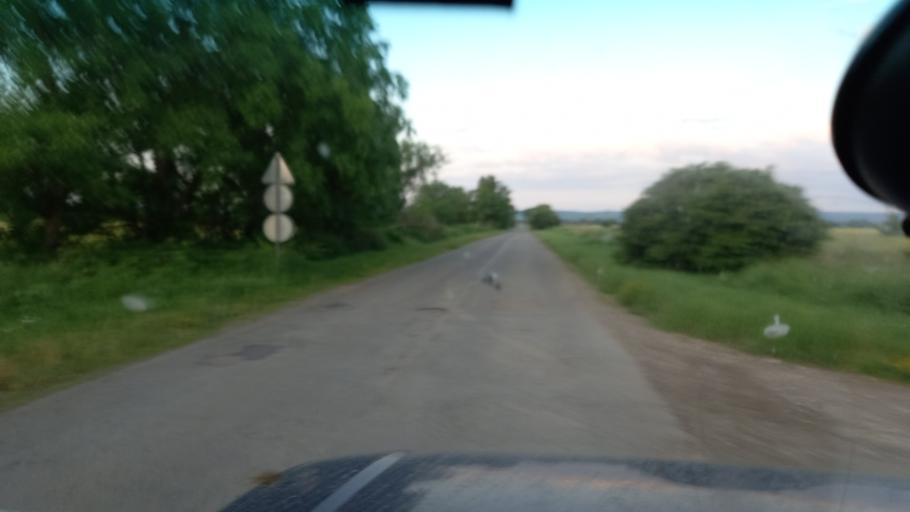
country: RU
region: Krasnodarskiy
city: Mostovskoy
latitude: 44.4231
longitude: 40.7500
